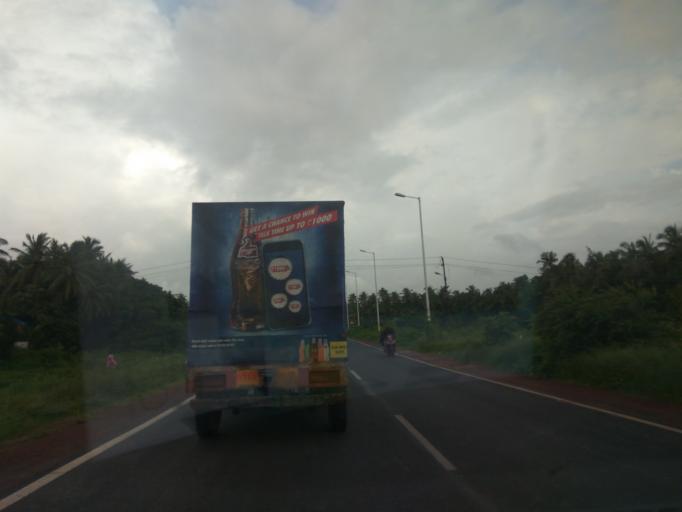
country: IN
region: Goa
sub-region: North Goa
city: Goa Velha
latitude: 15.4375
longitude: 73.8815
